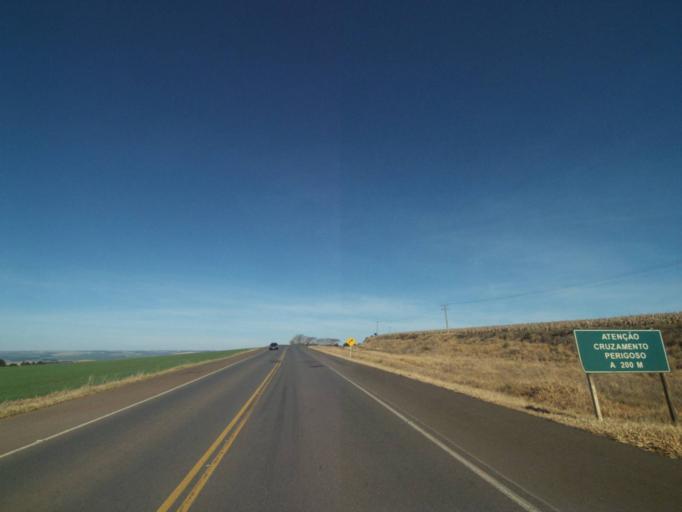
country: BR
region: Parana
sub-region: Tibagi
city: Tibagi
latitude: -24.3932
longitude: -50.3362
